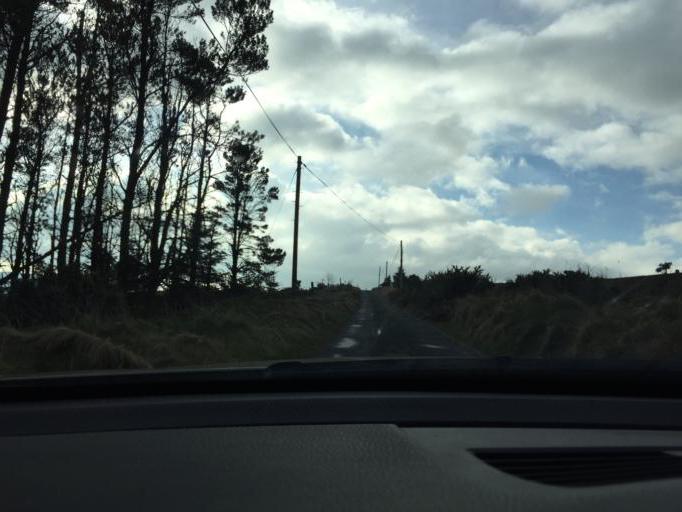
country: IE
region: Leinster
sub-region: Wicklow
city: Valleymount
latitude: 53.0728
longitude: -6.4910
